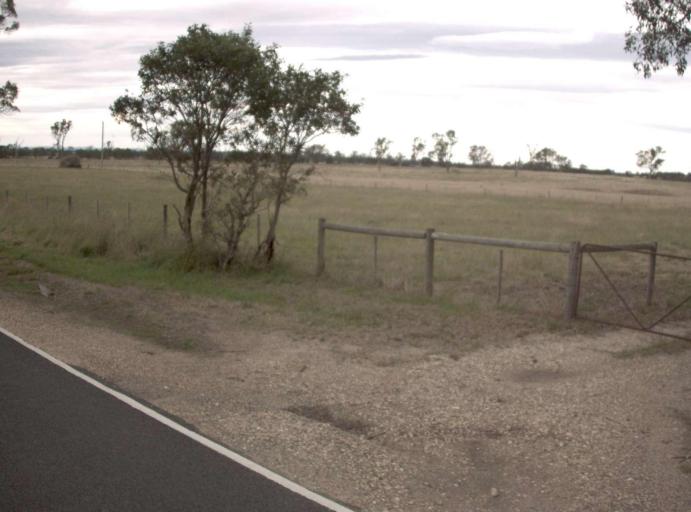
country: AU
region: Victoria
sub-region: Wellington
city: Sale
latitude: -37.9976
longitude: 147.1918
